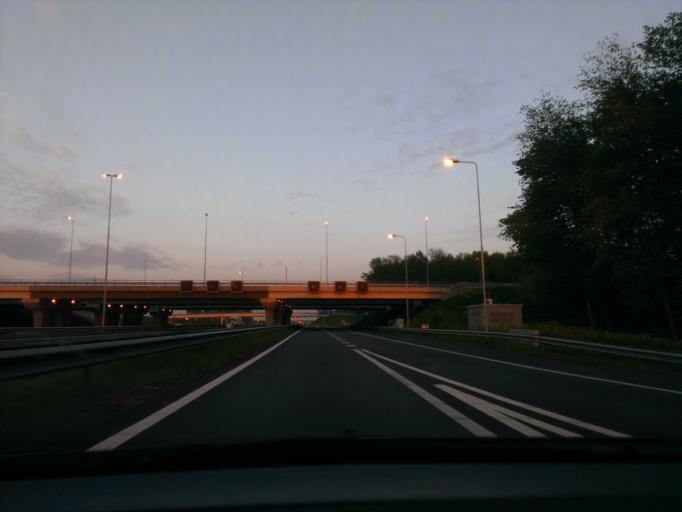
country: NL
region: Gelderland
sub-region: Gemeente Overbetuwe
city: Herveld
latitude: 51.9086
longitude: 5.7661
